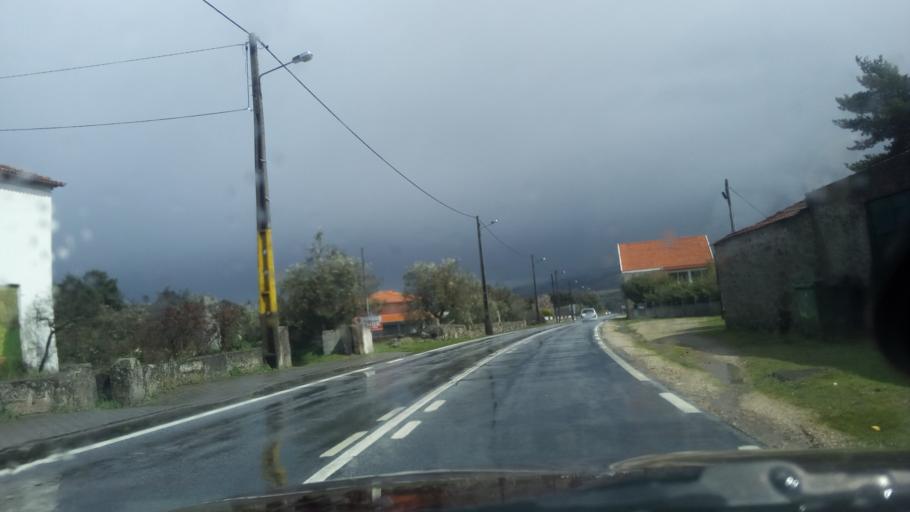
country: PT
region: Guarda
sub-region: Fornos de Algodres
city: Fornos de Algodres
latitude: 40.5600
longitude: -7.4835
